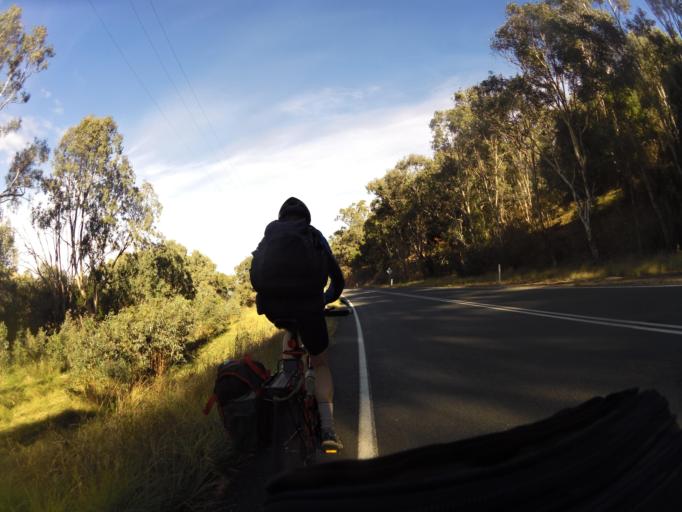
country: AU
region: New South Wales
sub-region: Greater Hume Shire
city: Holbrook
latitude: -35.9788
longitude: 147.8146
